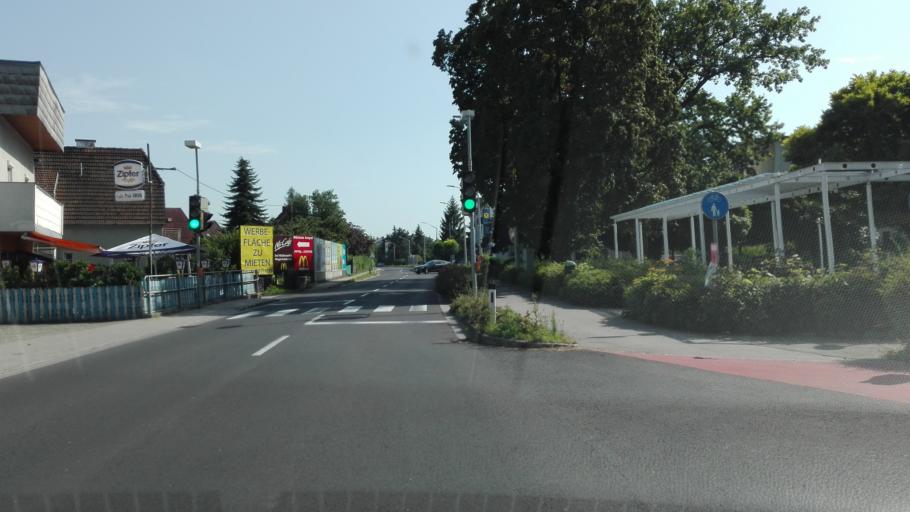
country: AT
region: Upper Austria
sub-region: Politischer Bezirk Linz-Land
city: Leonding
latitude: 48.2515
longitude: 14.2598
